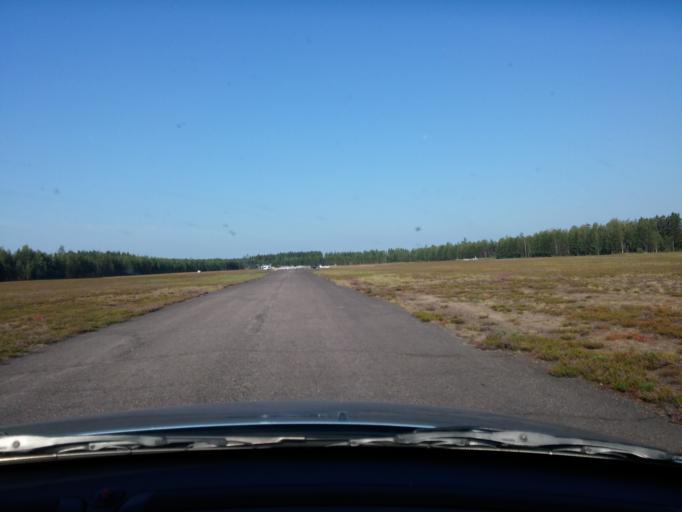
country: FI
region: Uusimaa
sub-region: Helsinki
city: Kaerkoelae
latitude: 60.7419
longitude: 24.1072
